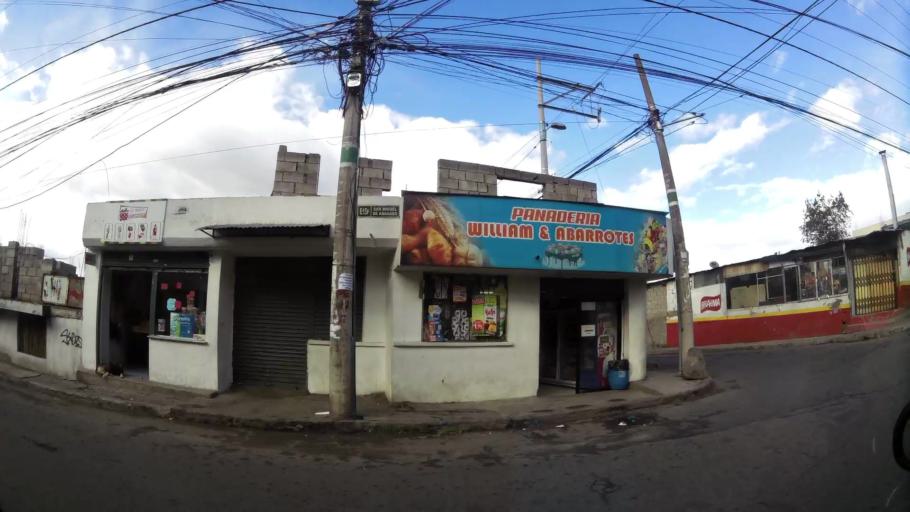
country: EC
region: Pichincha
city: Quito
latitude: -0.1358
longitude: -78.4610
